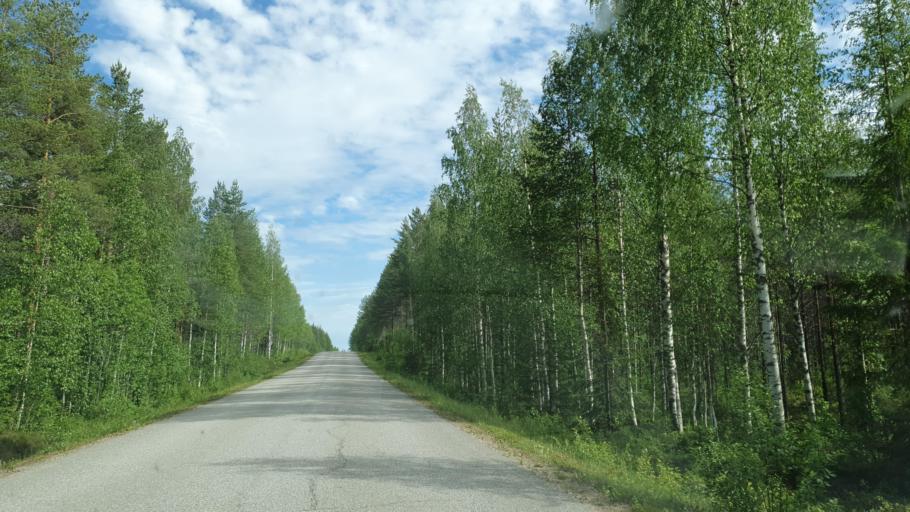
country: FI
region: Kainuu
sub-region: Kehys-Kainuu
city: Kuhmo
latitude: 64.5432
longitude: 29.2597
